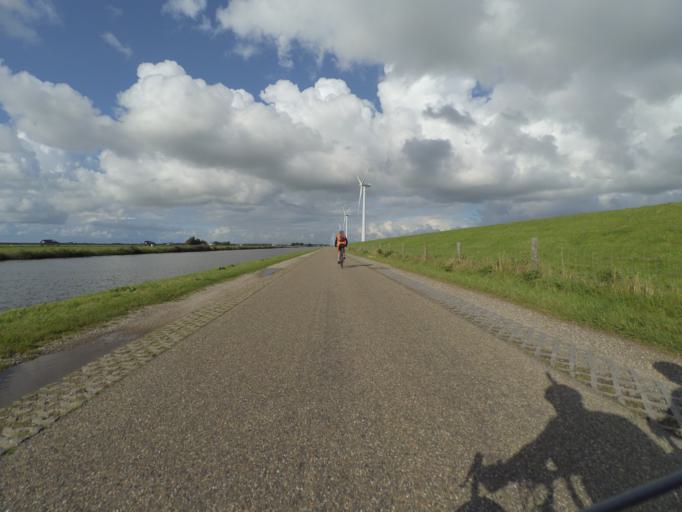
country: NL
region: North Holland
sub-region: Gemeente Schagen
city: Schagen
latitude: 52.8563
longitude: 4.7622
